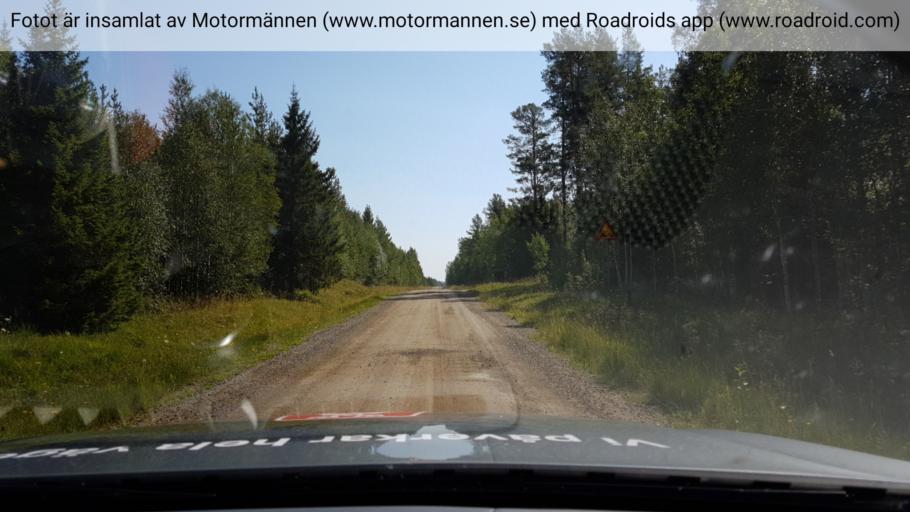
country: SE
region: Jaemtland
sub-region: Stroemsunds Kommun
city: Stroemsund
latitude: 63.3110
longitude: 15.5271
